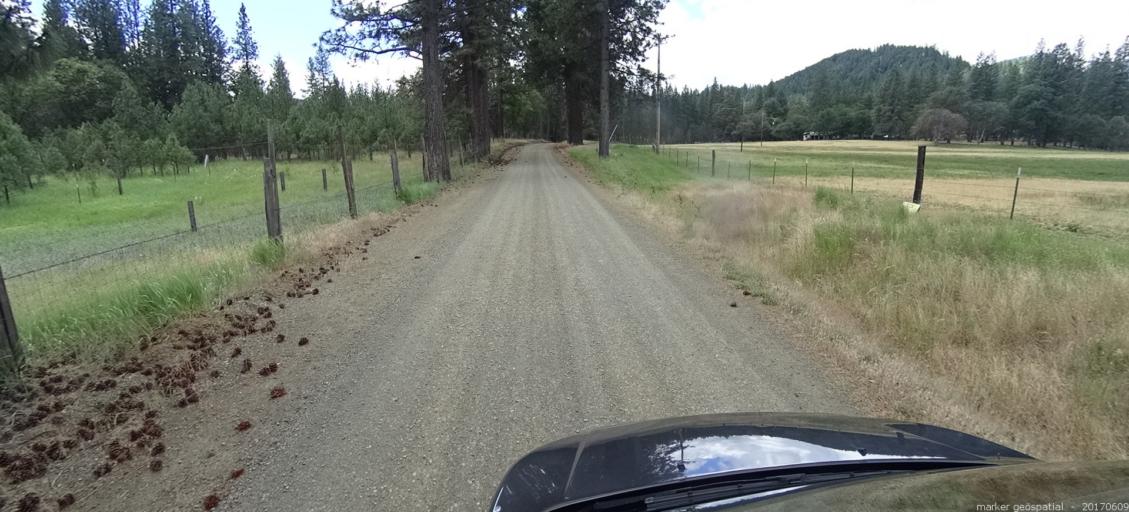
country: US
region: California
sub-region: Siskiyou County
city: Yreka
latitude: 41.3797
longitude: -122.8713
